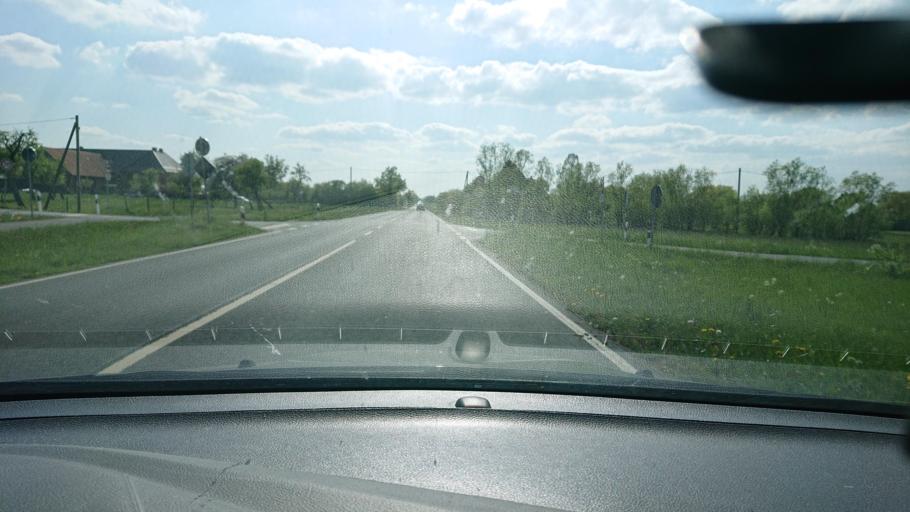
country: DE
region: North Rhine-Westphalia
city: Oelde
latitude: 51.7943
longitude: 8.1678
